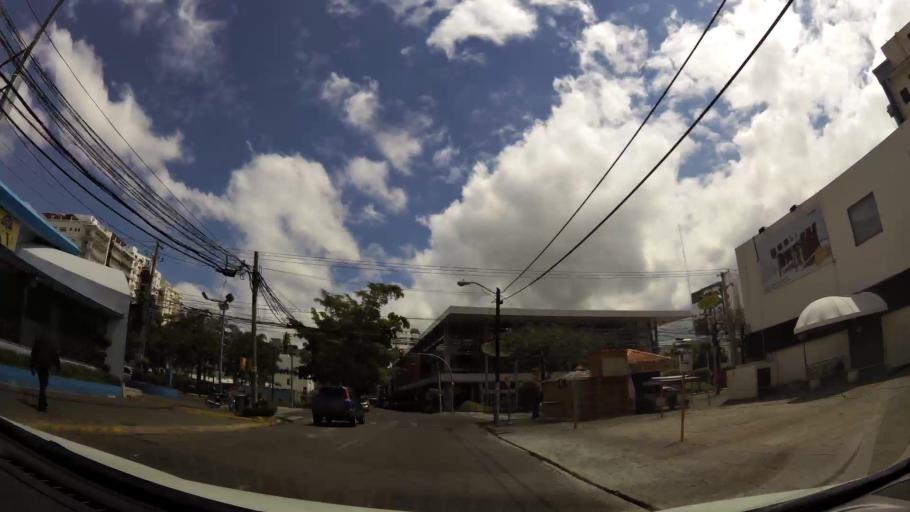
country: DO
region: Nacional
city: La Julia
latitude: 18.4725
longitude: -69.9259
